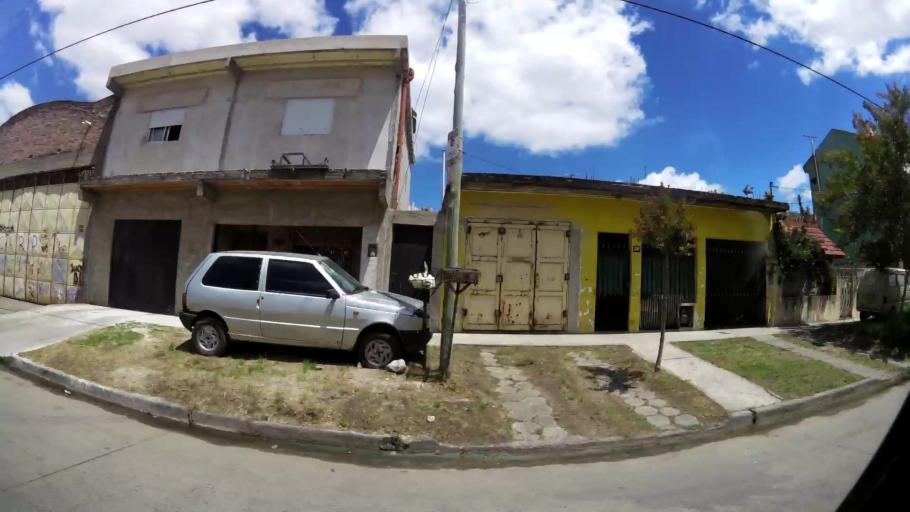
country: AR
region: Buenos Aires
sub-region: Partido de Lanus
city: Lanus
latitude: -34.7088
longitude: -58.4266
